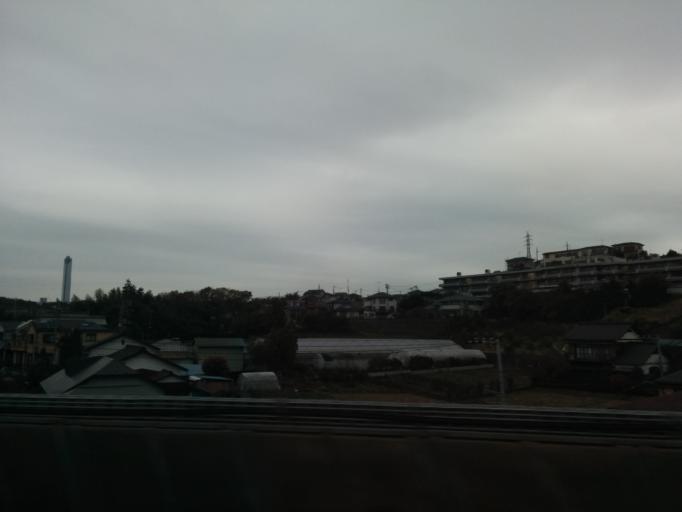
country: JP
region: Kanagawa
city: Yokohama
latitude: 35.4787
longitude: 139.5661
